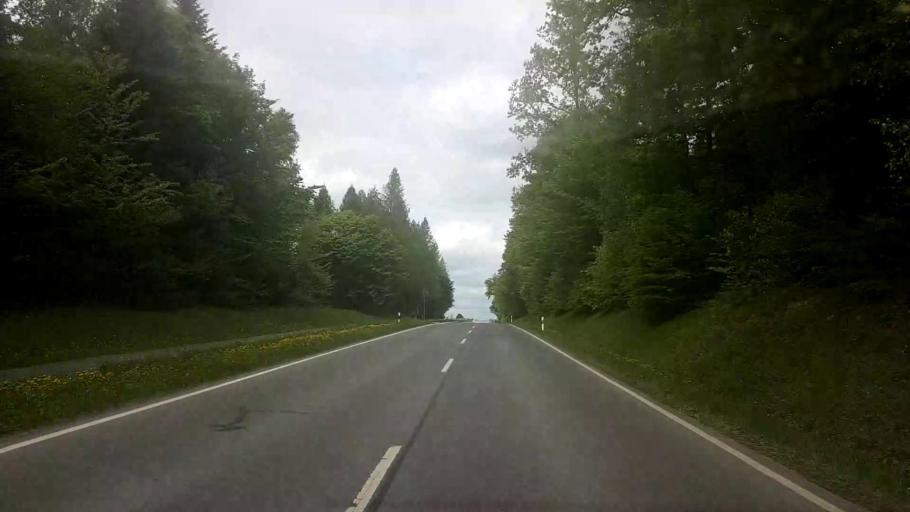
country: DE
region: Bavaria
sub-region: Upper Franconia
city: Lichtenfels
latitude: 50.1750
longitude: 11.0224
